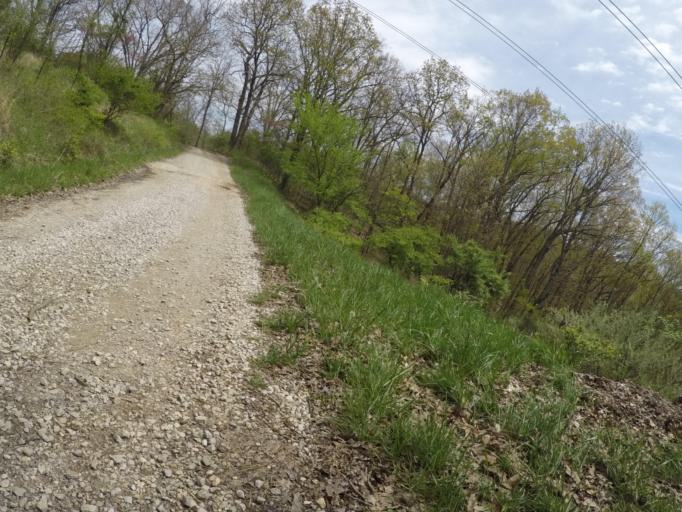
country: US
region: West Virginia
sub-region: Wayne County
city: Lavalette
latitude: 38.3671
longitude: -82.4827
